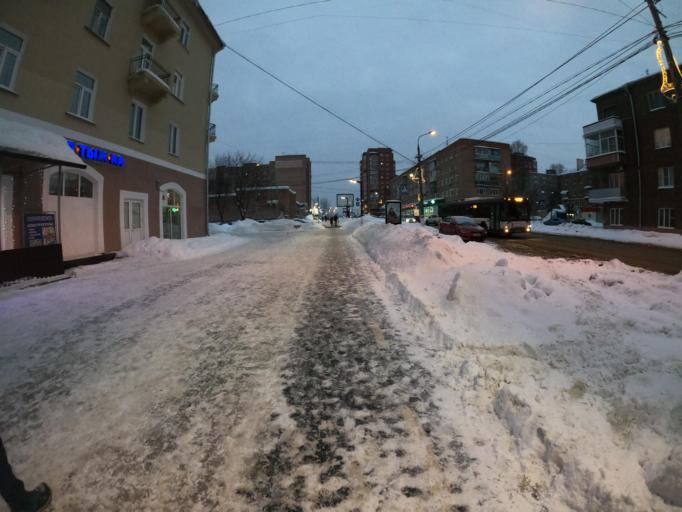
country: RU
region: Moskovskaya
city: Pavlovskiy Posad
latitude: 55.7791
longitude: 38.6715
